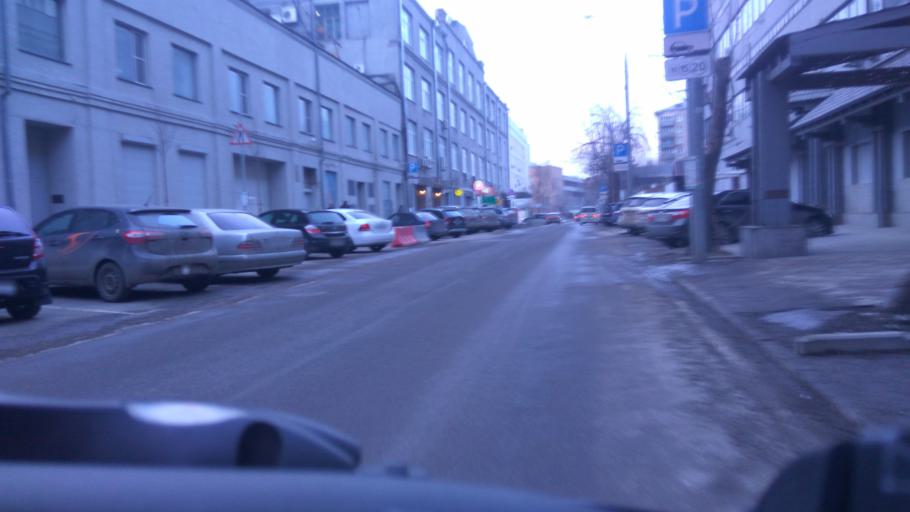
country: RU
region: Moskovskaya
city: Presnenskiy
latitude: 55.7619
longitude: 37.5549
